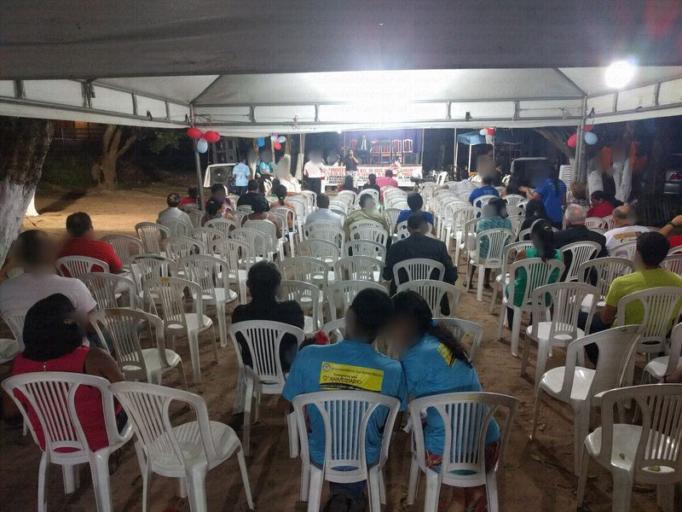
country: BR
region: Rio Grande do Norte
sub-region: Ares
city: Ares
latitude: -6.2328
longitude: -35.0457
